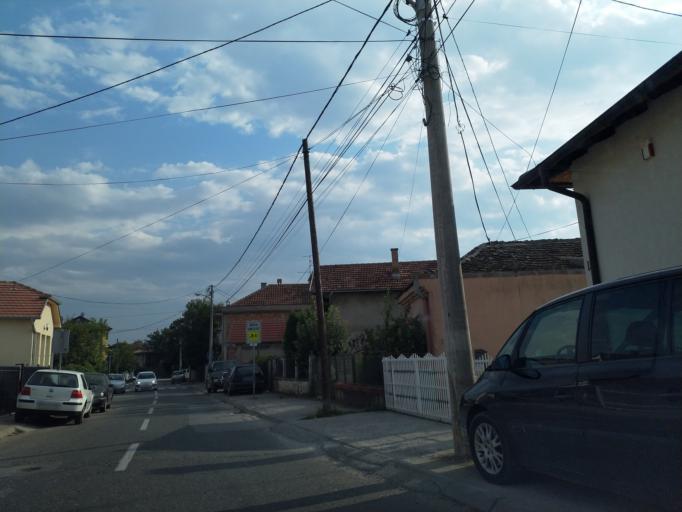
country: RS
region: Central Serbia
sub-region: Pomoravski Okrug
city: Paracin
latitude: 43.8659
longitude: 21.4130
